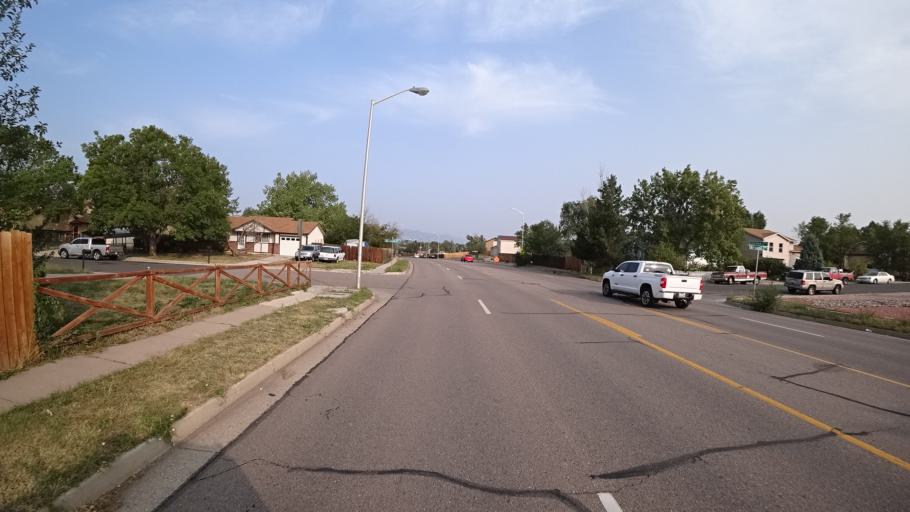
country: US
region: Colorado
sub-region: El Paso County
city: Stratmoor
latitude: 38.8033
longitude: -104.7443
